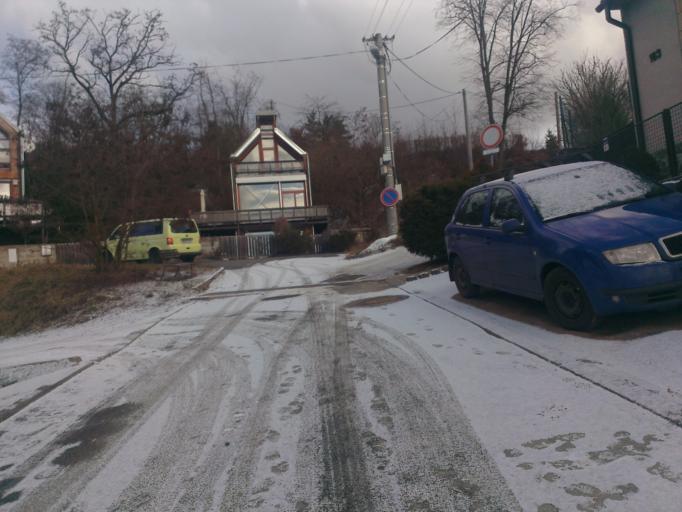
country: CZ
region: South Moravian
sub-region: Okres Brno-Venkov
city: Lelekovice
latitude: 49.2913
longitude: 16.5860
